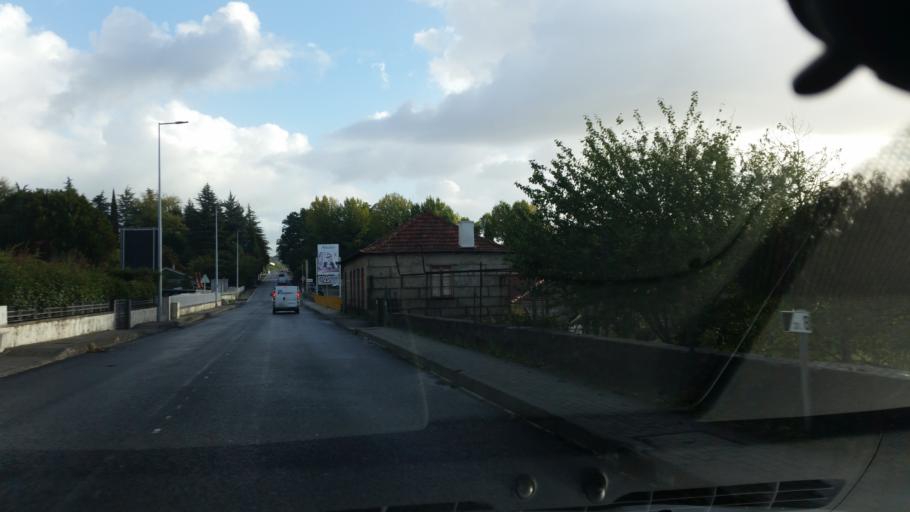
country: PT
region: Porto
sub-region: Santo Tirso
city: Aves
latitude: 41.3640
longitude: -8.3962
